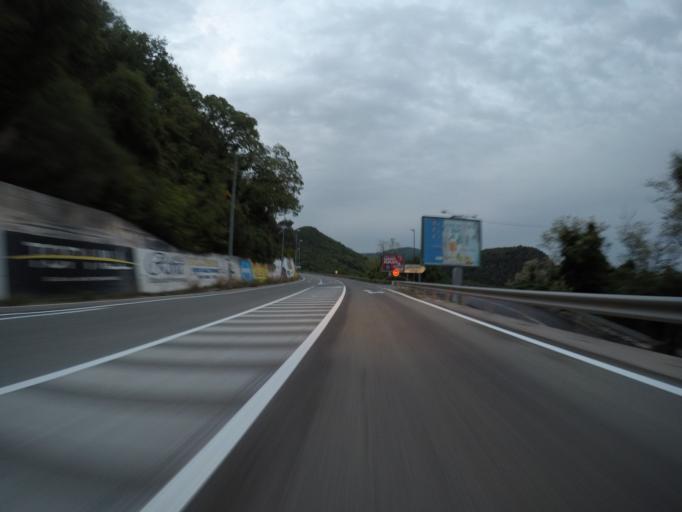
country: ME
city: Petrovac na Moru
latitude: 42.2046
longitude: 18.9507
